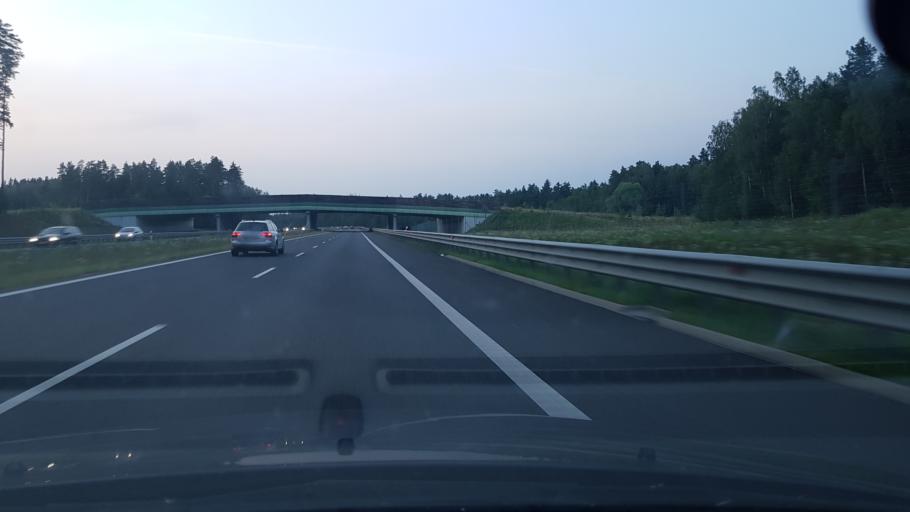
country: PL
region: Warmian-Masurian Voivodeship
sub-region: Powiat olsztynski
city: Olsztynek
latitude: 53.4587
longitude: 20.3217
